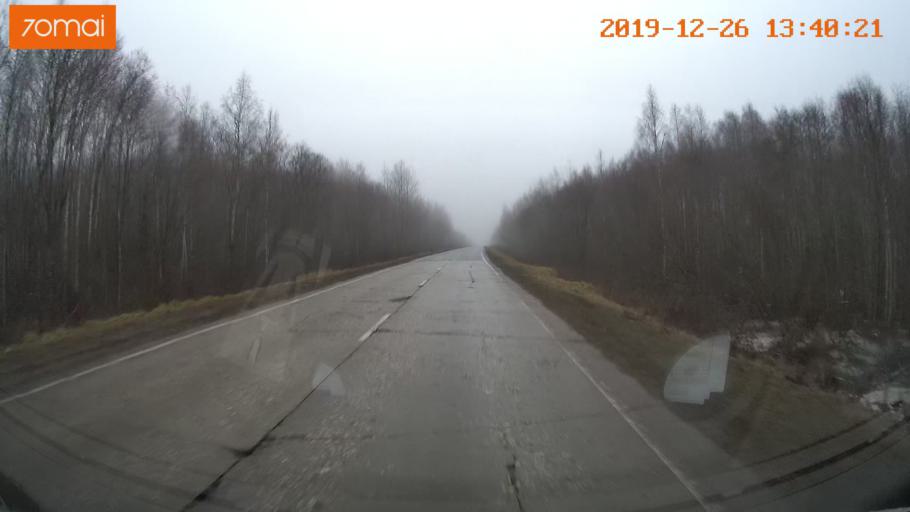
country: RU
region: Vologda
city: Sheksna
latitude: 58.7434
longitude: 38.4279
